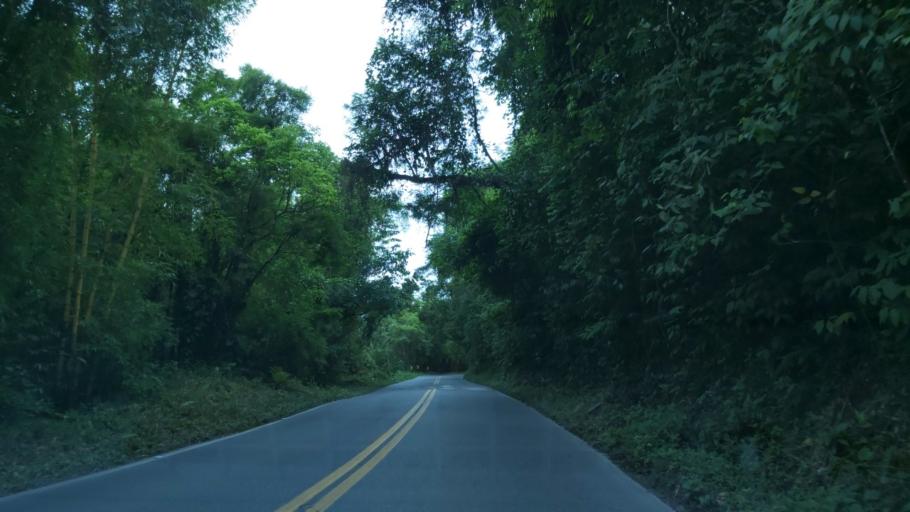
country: BR
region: Sao Paulo
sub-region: Juquia
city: Juquia
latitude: -24.1106
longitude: -47.6291
